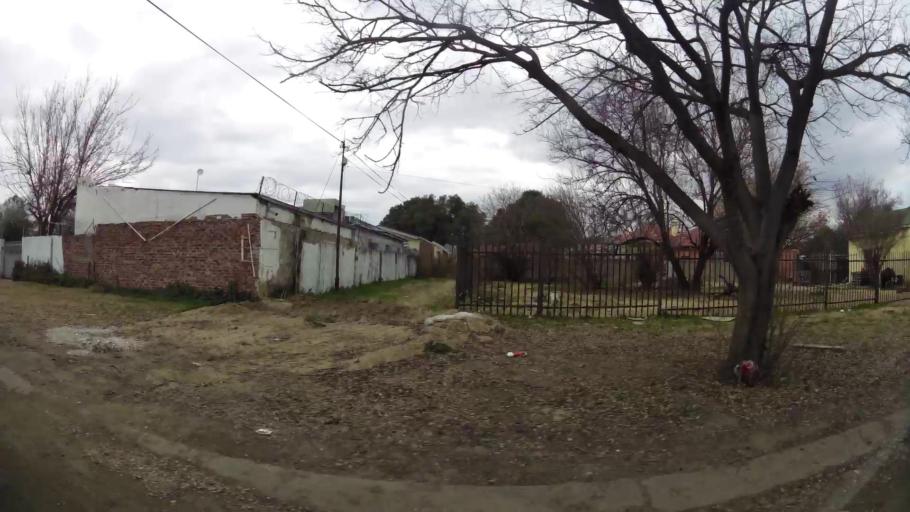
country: ZA
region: Orange Free State
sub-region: Fezile Dabi District Municipality
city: Kroonstad
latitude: -27.6599
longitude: 27.2426
